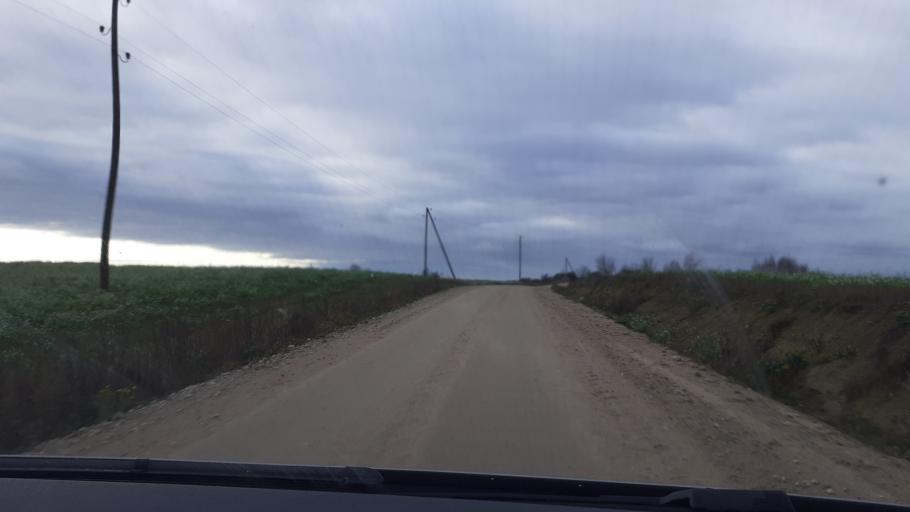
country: LV
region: Aizpute
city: Aizpute
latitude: 56.7671
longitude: 21.8030
